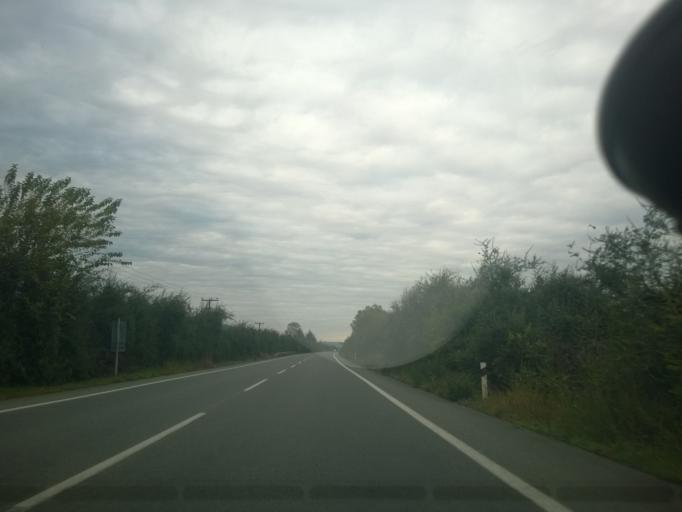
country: GR
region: Central Macedonia
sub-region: Nomos Pellis
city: Kali
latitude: 40.8055
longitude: 22.2034
